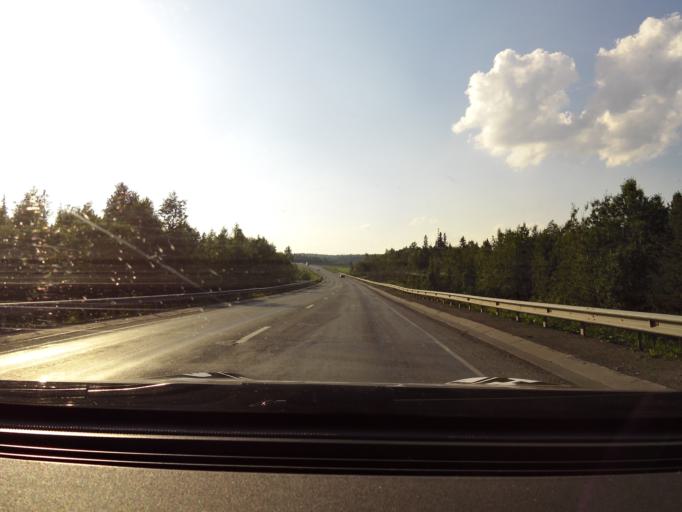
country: RU
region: Sverdlovsk
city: Revda
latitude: 56.8446
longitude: 59.8213
